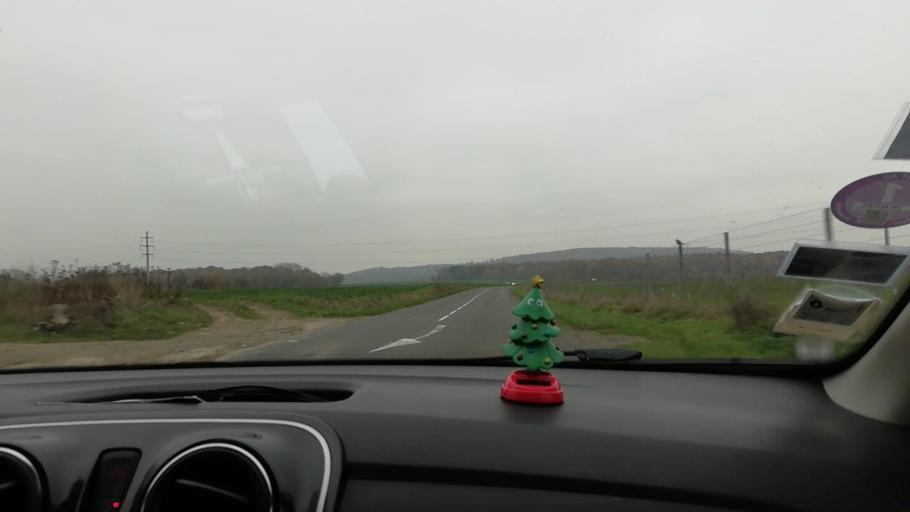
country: FR
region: Ile-de-France
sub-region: Departement de Seine-et-Marne
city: Saint-Mard
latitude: 49.0411
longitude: 2.7105
